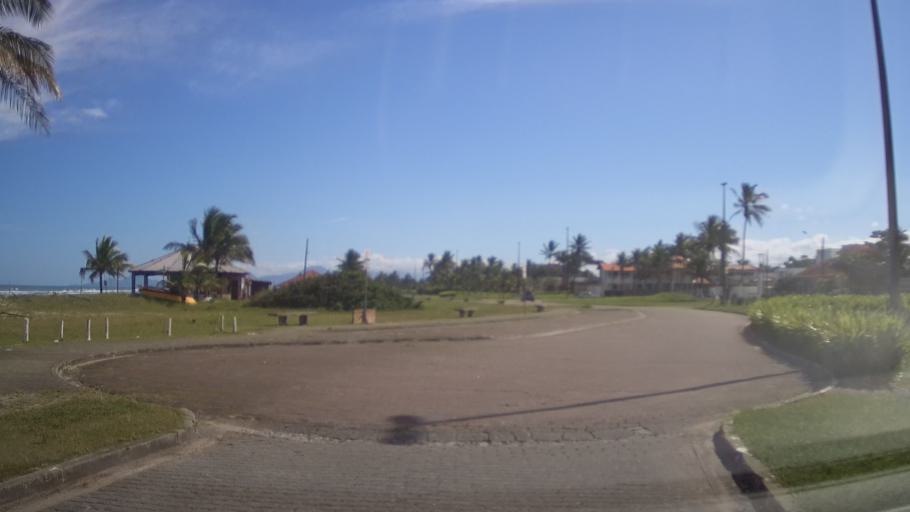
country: BR
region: Sao Paulo
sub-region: Itanhaem
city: Itanhaem
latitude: -24.2012
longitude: -46.8175
